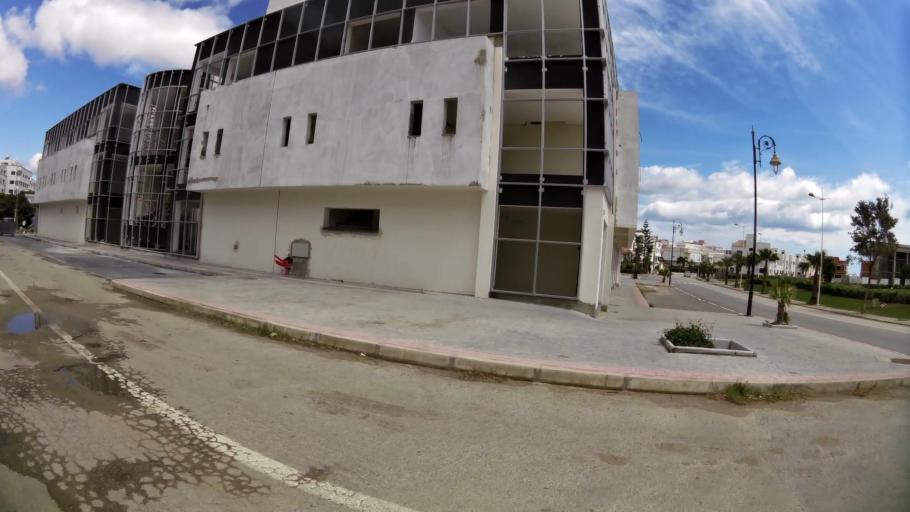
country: MA
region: Tanger-Tetouan
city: Tetouan
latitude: 35.5861
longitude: -5.3379
